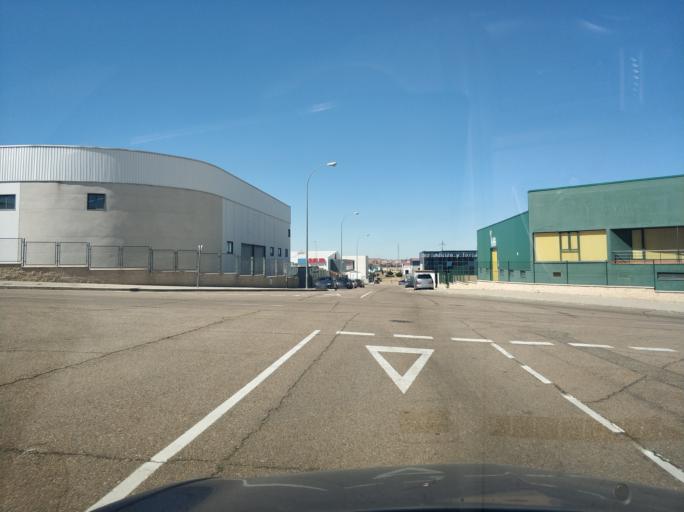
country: ES
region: Castille and Leon
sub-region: Provincia de Salamanca
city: Carbajosa de la Sagrada
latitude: 40.9383
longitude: -5.6579
